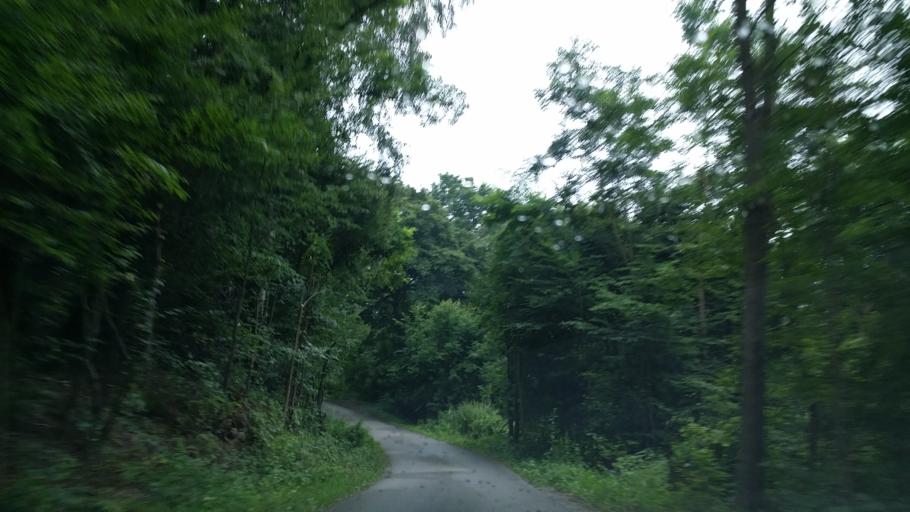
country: PL
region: Lesser Poland Voivodeship
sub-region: Powiat wadowicki
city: Spytkowice
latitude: 49.9808
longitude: 19.5063
